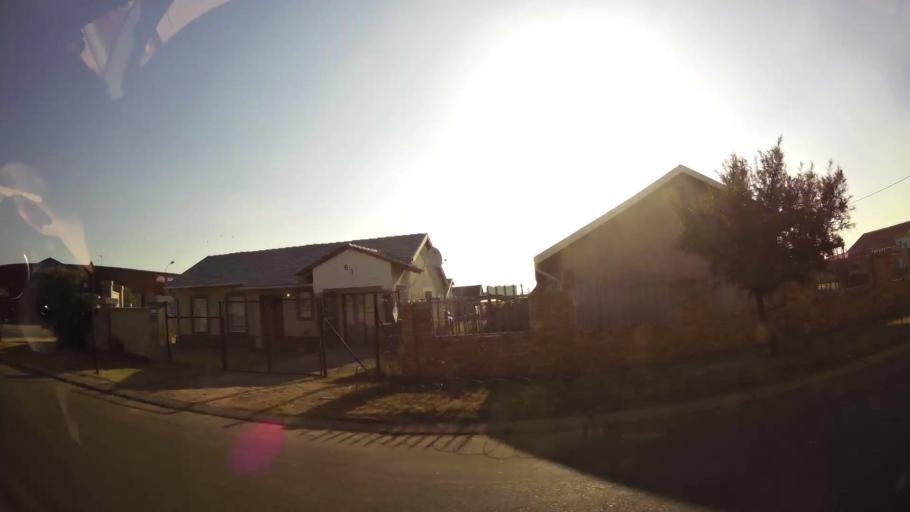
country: ZA
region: Gauteng
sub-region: West Rand District Municipality
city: Randfontein
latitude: -26.1919
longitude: 27.6997
